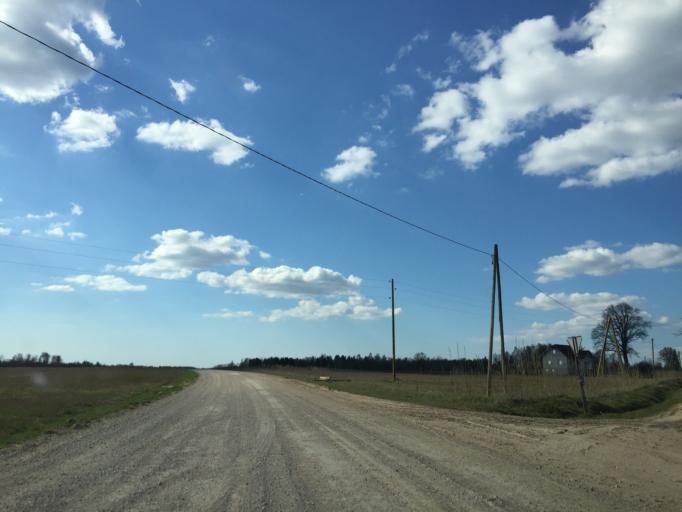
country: LV
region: Krimulda
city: Ragana
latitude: 57.3367
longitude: 24.6389
